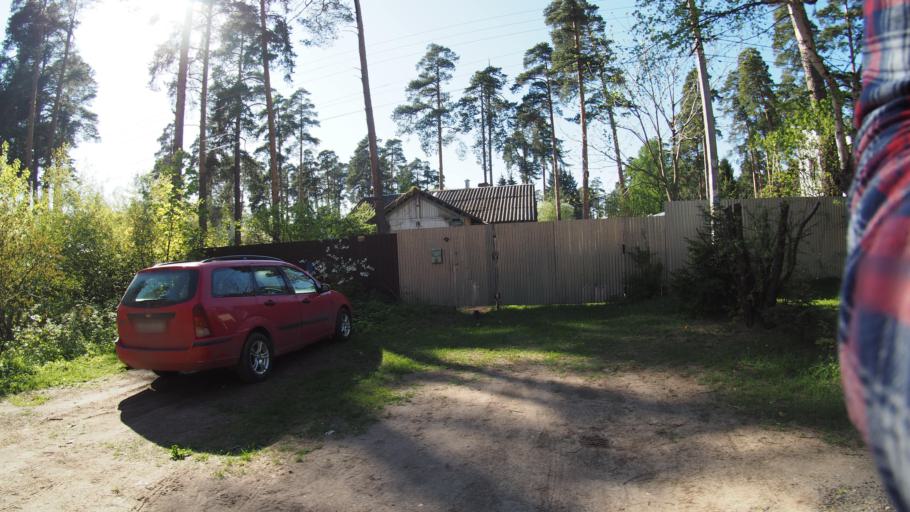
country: RU
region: Moskovskaya
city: Kratovo
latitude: 55.5750
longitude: 38.1806
